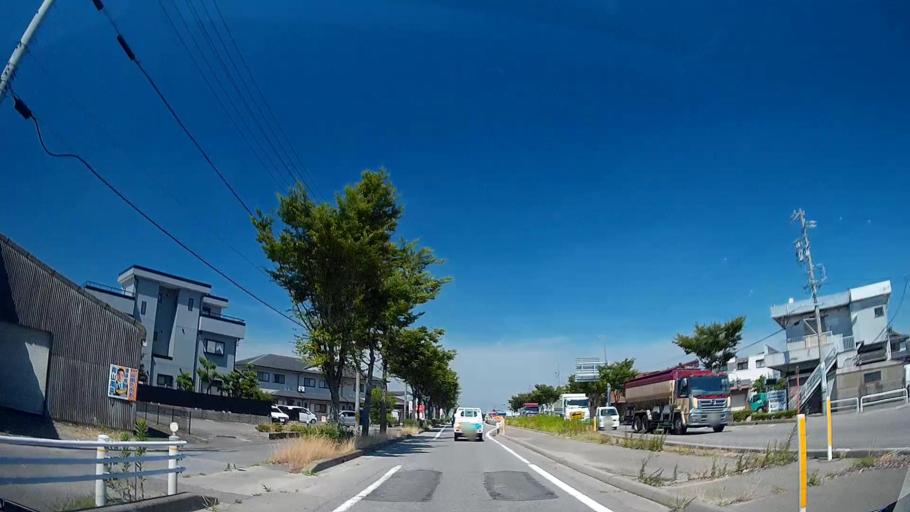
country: JP
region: Aichi
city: Nishio
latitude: 34.8483
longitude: 137.0259
